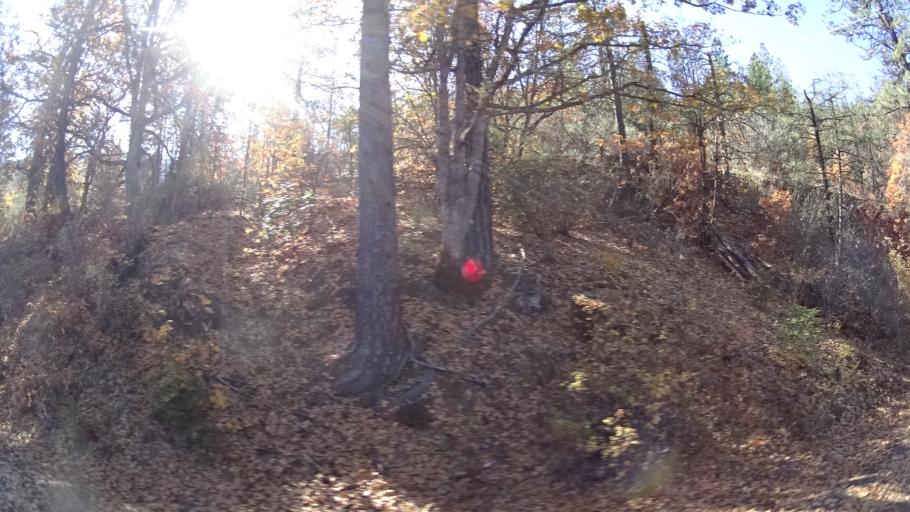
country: US
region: California
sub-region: Siskiyou County
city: Yreka
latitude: 41.8423
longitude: -122.8952
